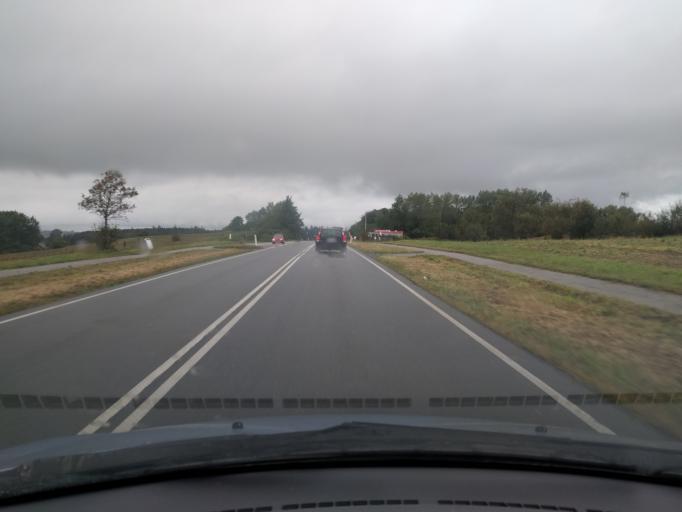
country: DK
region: Zealand
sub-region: Naestved Kommune
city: Naestved
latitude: 55.1450
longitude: 11.8182
